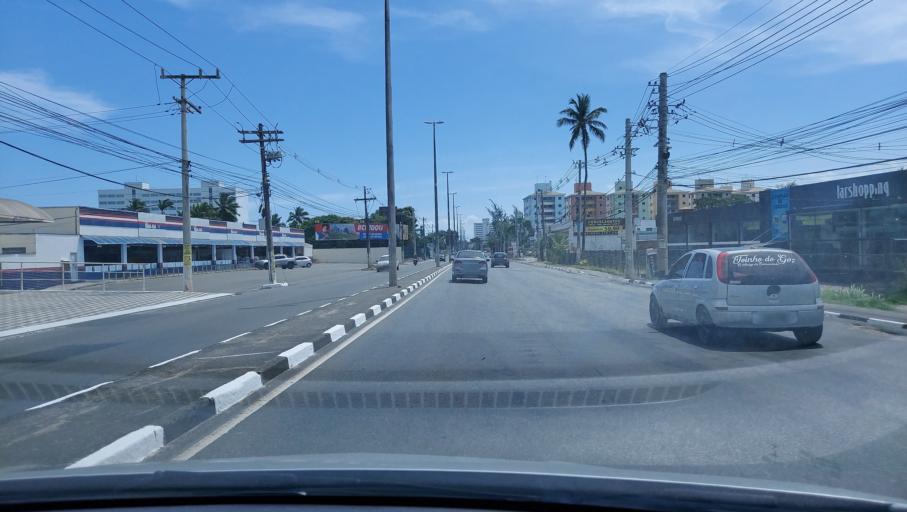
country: BR
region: Bahia
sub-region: Lauro De Freitas
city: Lauro de Freitas
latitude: -12.8943
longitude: -38.3279
